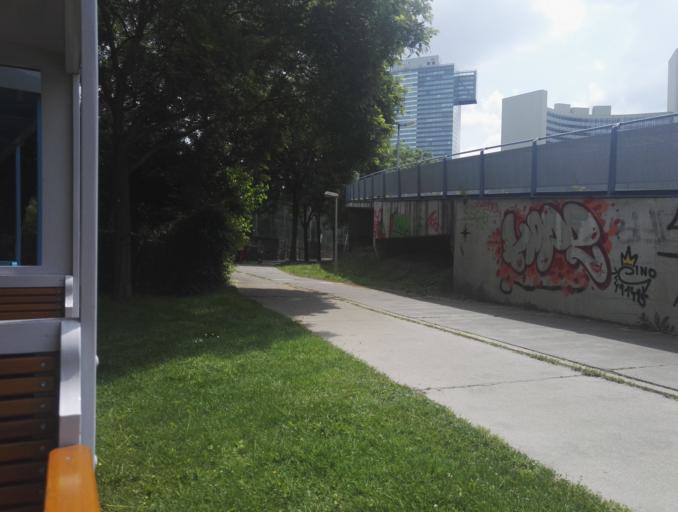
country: AT
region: Vienna
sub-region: Wien Stadt
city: Vienna
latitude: 48.2371
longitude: 16.4163
